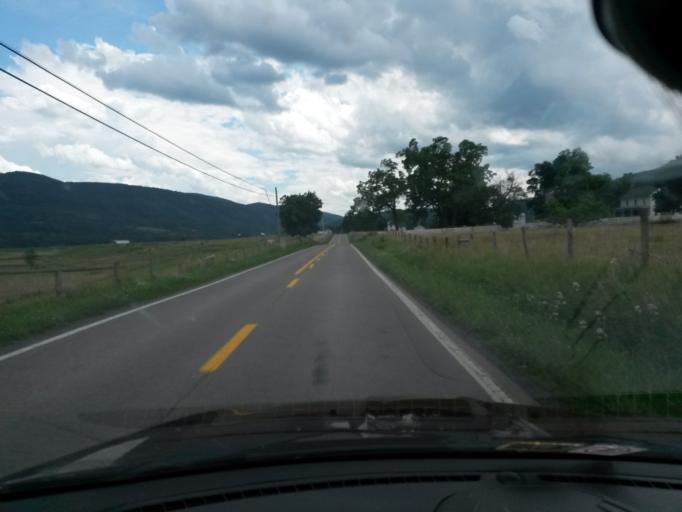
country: US
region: West Virginia
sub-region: Pendleton County
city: Franklin
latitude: 38.7720
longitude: -79.2848
